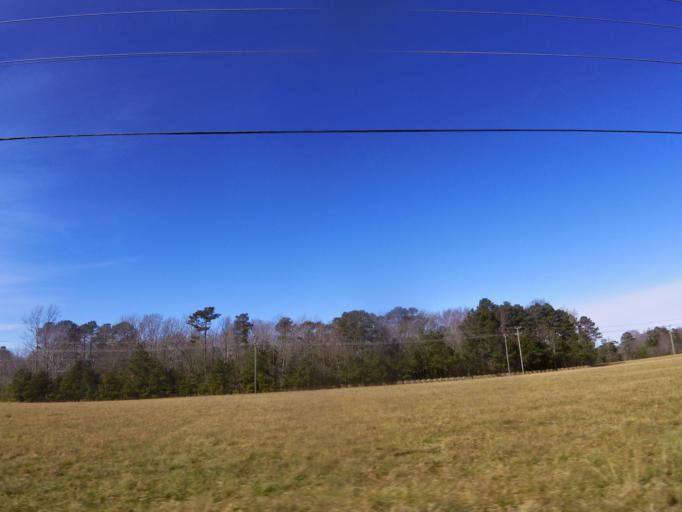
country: US
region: Virginia
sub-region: Isle of Wight County
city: Smithfield
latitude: 36.9679
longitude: -76.6593
